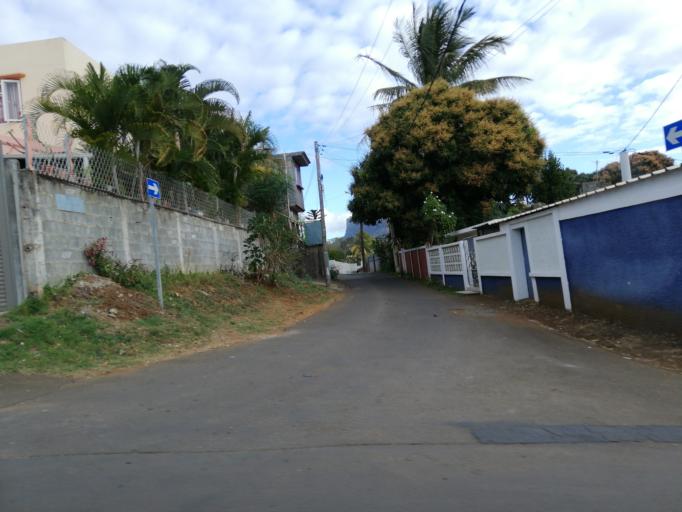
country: MU
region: Black River
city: Petite Riviere
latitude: -20.2212
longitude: 57.4601
